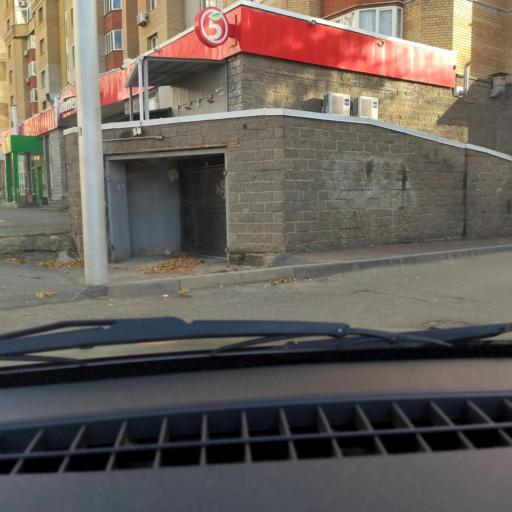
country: RU
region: Bashkortostan
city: Ufa
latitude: 54.7295
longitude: 55.9269
